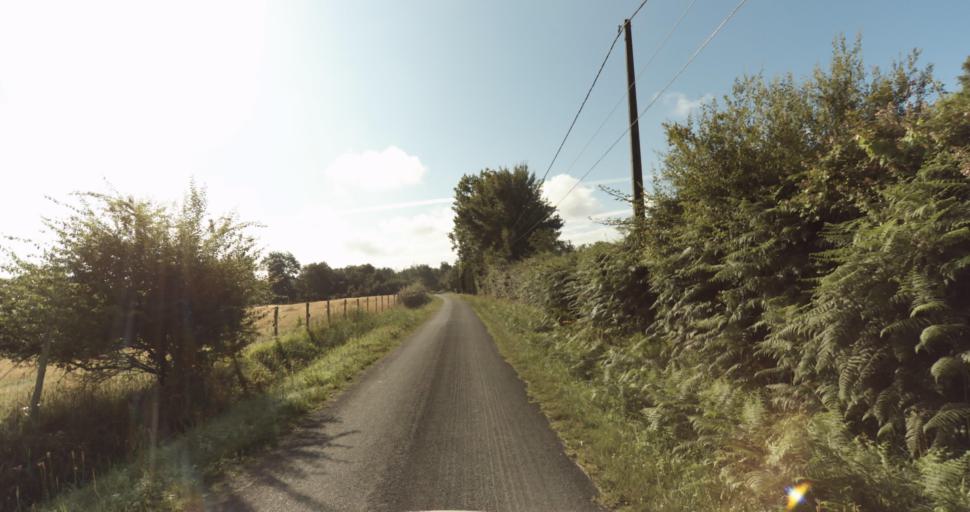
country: FR
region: Aquitaine
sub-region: Departement de la Gironde
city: Bazas
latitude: 44.4282
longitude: -0.2528
